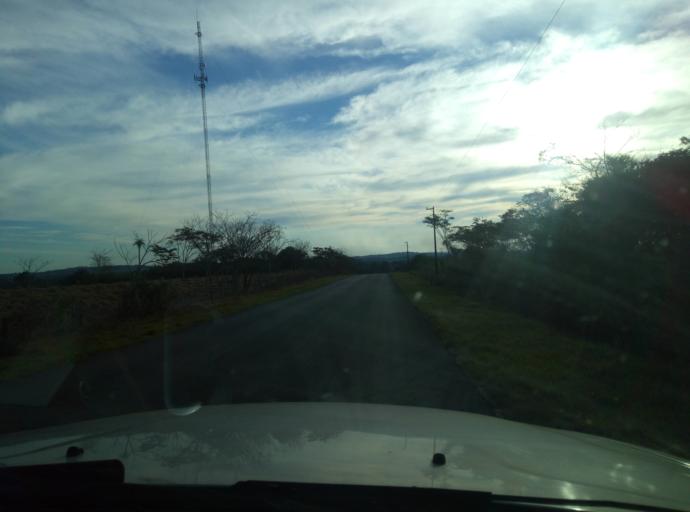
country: PY
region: Caaguazu
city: Carayao
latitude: -25.1530
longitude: -56.3256
